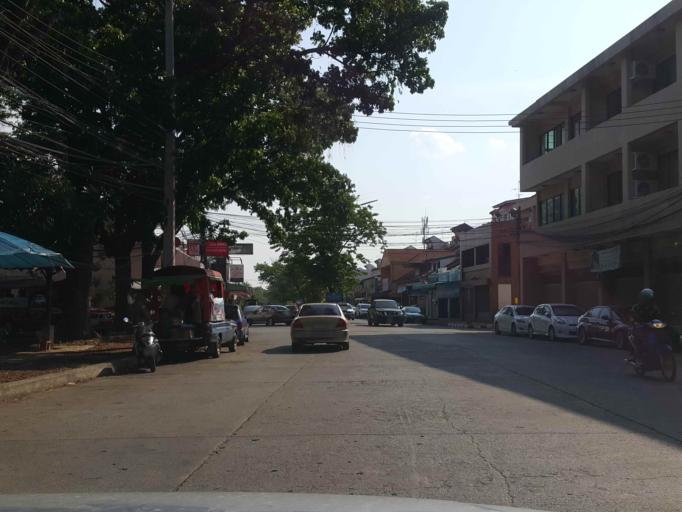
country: TH
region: Chiang Mai
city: Chiang Mai
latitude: 18.7685
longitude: 98.9979
